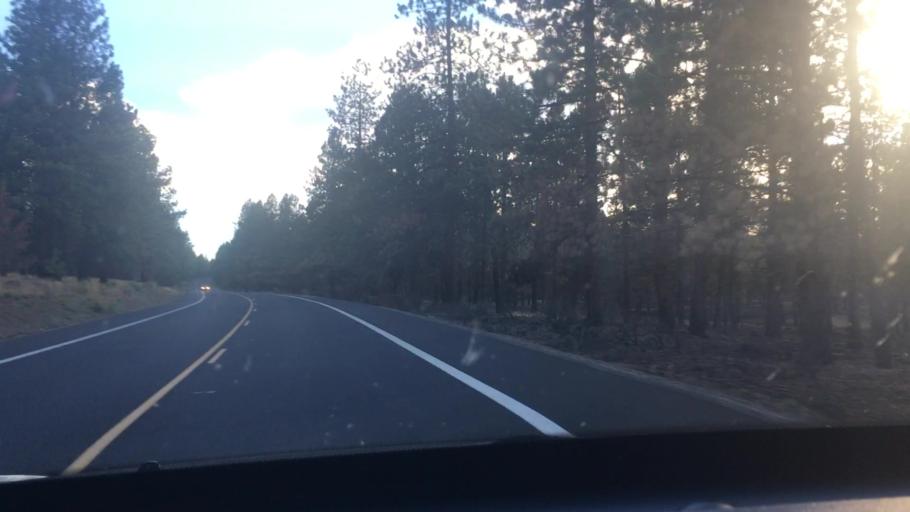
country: US
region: Oregon
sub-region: Deschutes County
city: Deschutes River Woods
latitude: 44.0487
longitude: -121.3916
